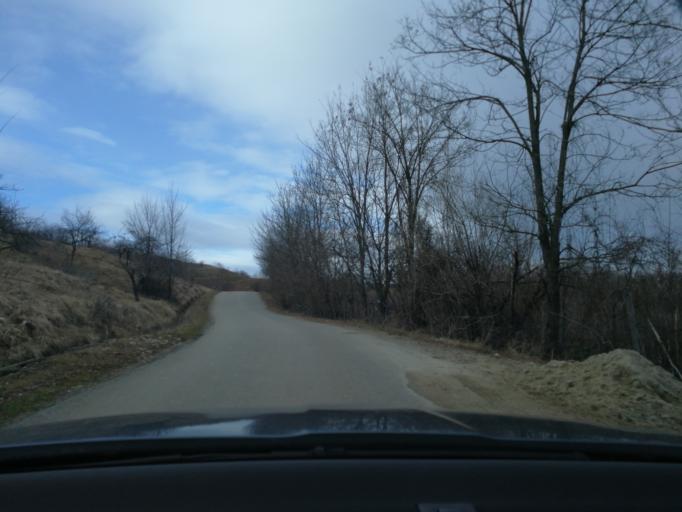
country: RO
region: Dambovita
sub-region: Comuna Buciumeni
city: Buciumeni
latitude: 45.1366
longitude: 25.4596
